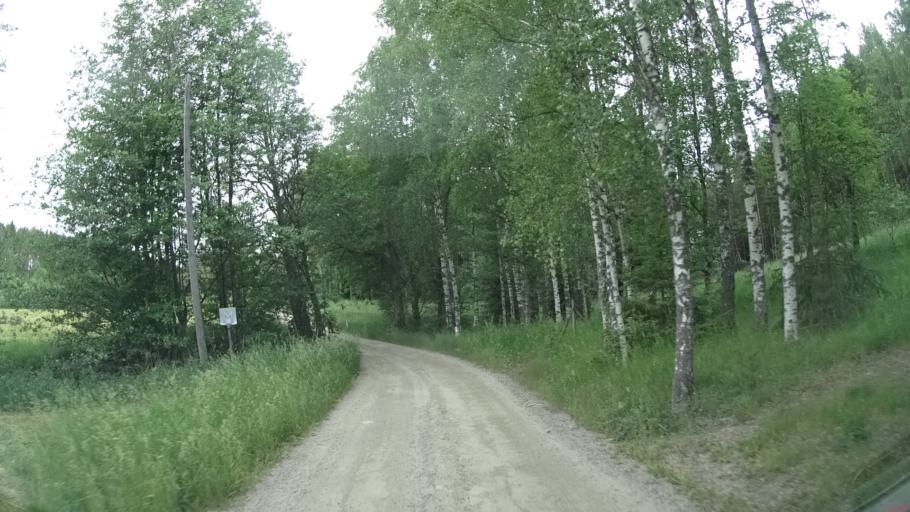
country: SE
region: Soedermanland
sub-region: Nykopings Kommun
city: Olstorp
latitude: 58.7646
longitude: 16.6930
